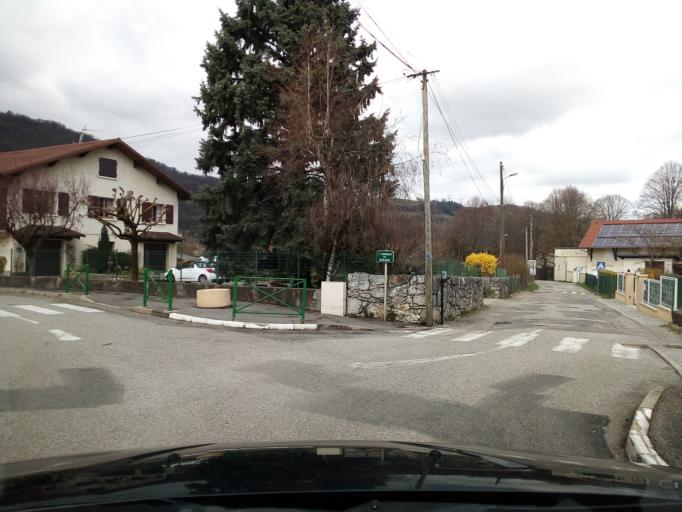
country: FR
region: Rhone-Alpes
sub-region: Departement de l'Isere
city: Chapareillan
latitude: 45.4684
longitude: 5.9892
